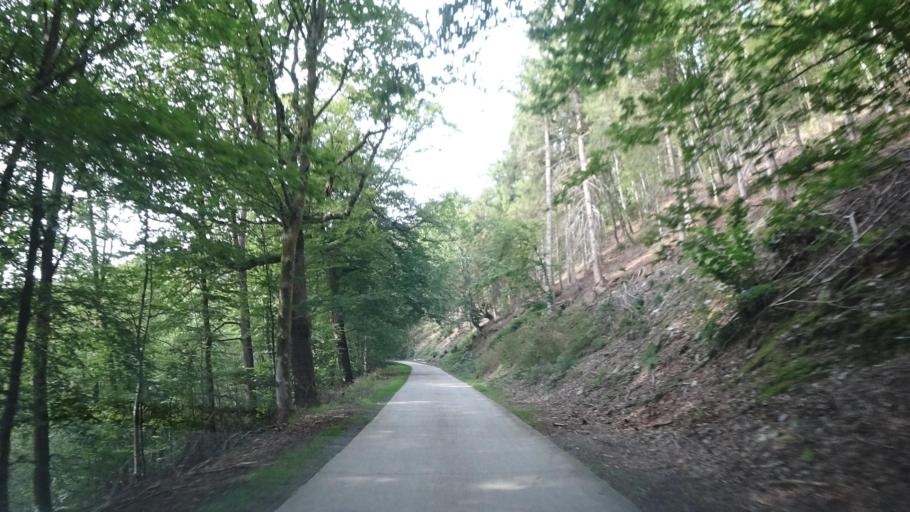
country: BE
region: Wallonia
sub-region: Province du Luxembourg
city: Herbeumont
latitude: 49.7703
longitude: 5.2495
